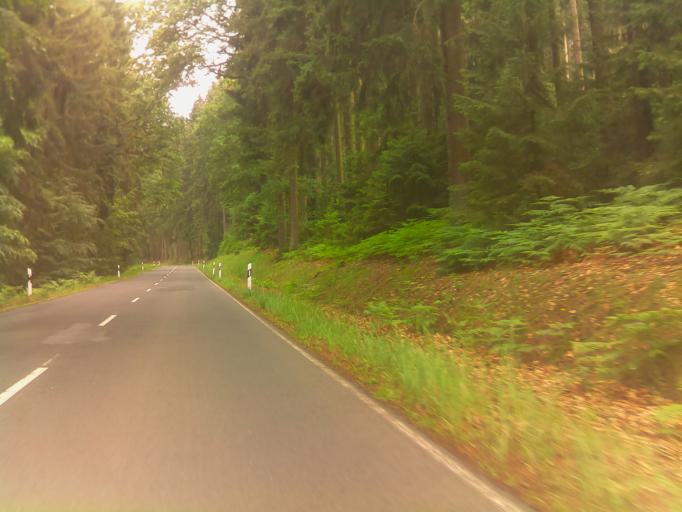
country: DE
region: Hesse
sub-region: Regierungsbezirk Darmstadt
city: Steinau an der Strasse
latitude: 50.2326
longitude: 9.4460
